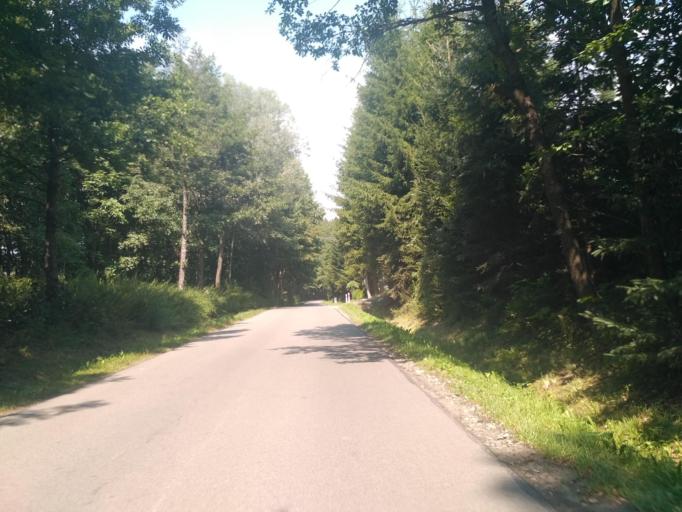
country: PL
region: Subcarpathian Voivodeship
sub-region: Powiat lancucki
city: Krzemienica
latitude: 50.0410
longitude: 22.1940
